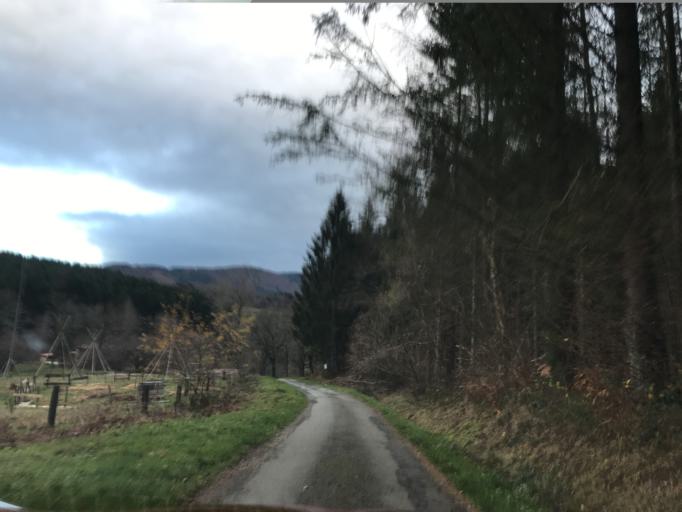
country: FR
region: Auvergne
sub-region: Departement du Puy-de-Dome
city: Celles-sur-Durolle
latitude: 45.8388
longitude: 3.6636
